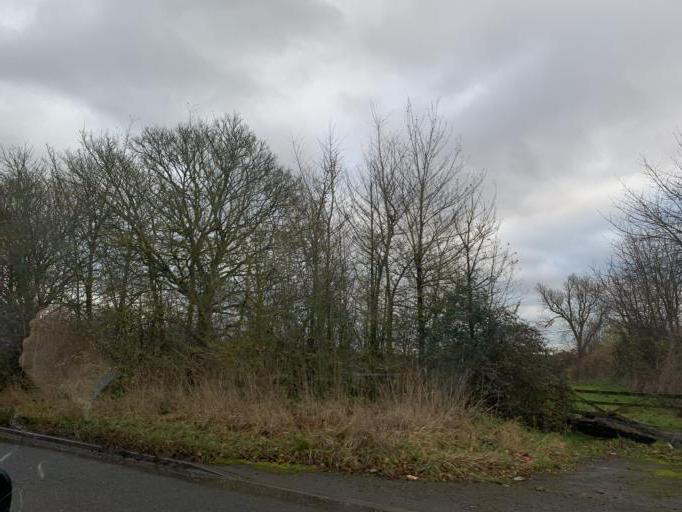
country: GB
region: England
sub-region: City of York
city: Bishopthorpe
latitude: 53.9261
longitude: -1.1209
